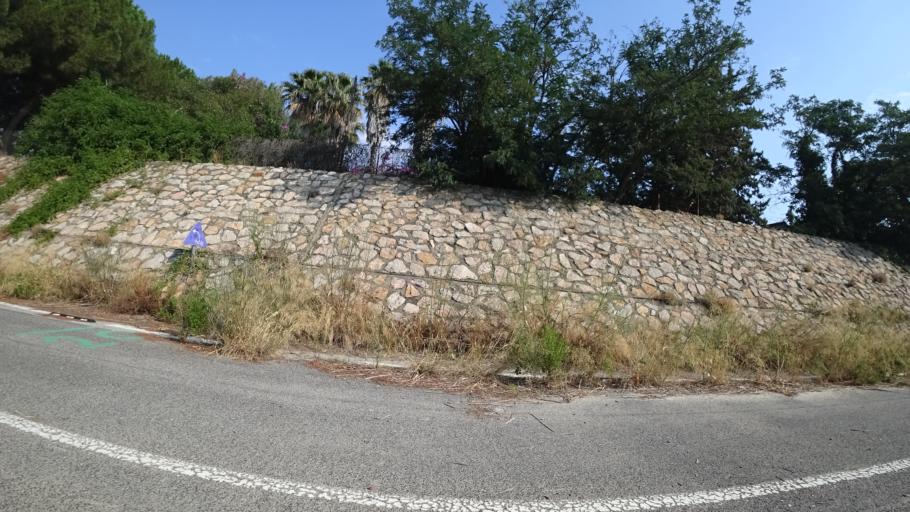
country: FR
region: Languedoc-Roussillon
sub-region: Departement des Pyrenees-Orientales
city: Perpignan
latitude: 42.7058
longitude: 2.8990
